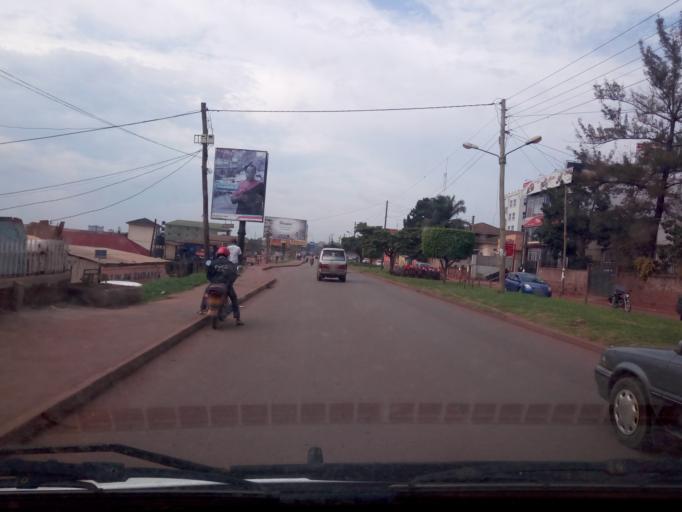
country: UG
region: Central Region
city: Kampala Central Division
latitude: 0.3402
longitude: 32.5874
